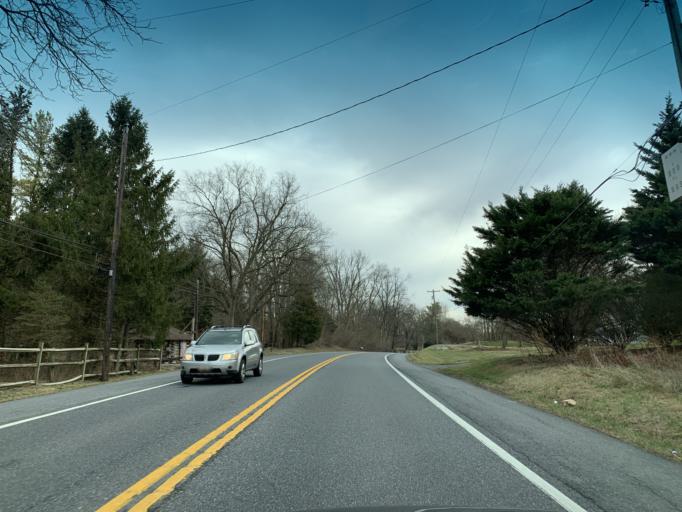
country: US
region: Maryland
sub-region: Washington County
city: Robinwood
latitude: 39.5817
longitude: -77.6938
